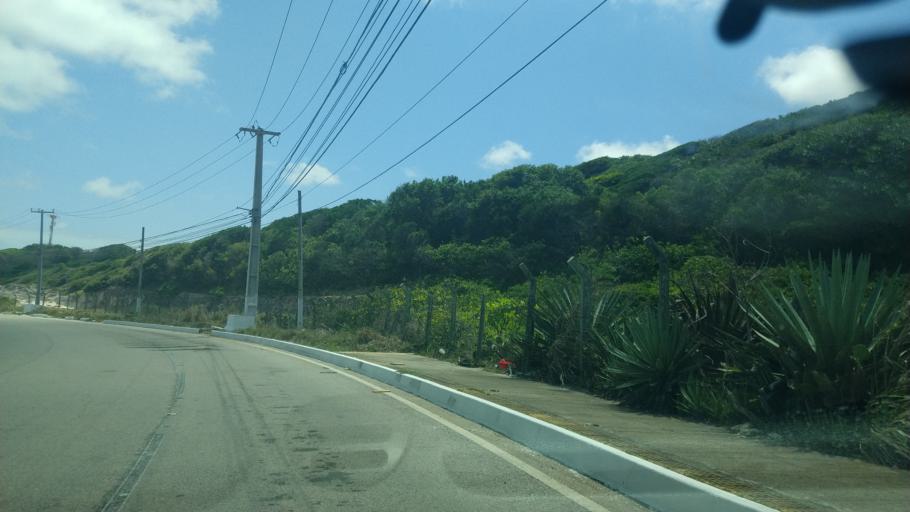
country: BR
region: Rio Grande do Norte
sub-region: Natal
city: Natal
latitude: -5.8080
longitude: -35.1832
